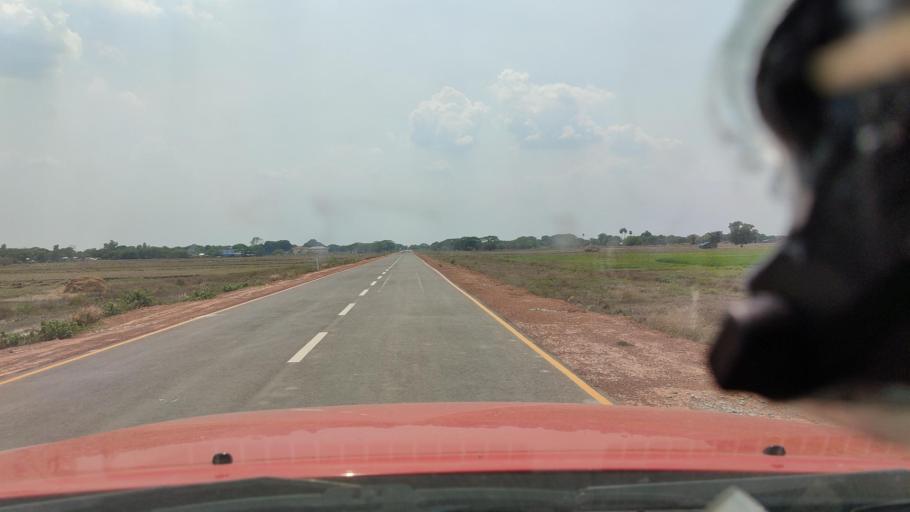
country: MM
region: Bago
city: Thanatpin
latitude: 17.0430
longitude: 96.3586
